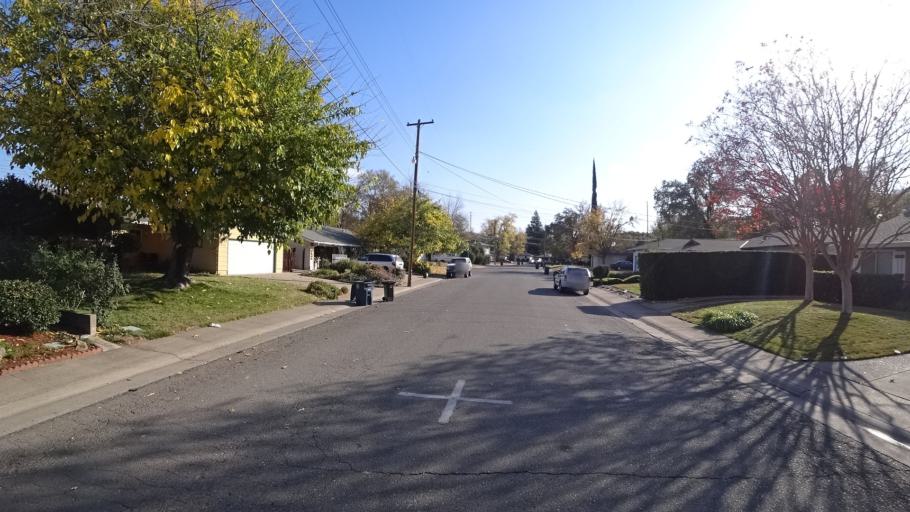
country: US
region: California
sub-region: Sacramento County
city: Citrus Heights
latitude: 38.6872
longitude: -121.2801
